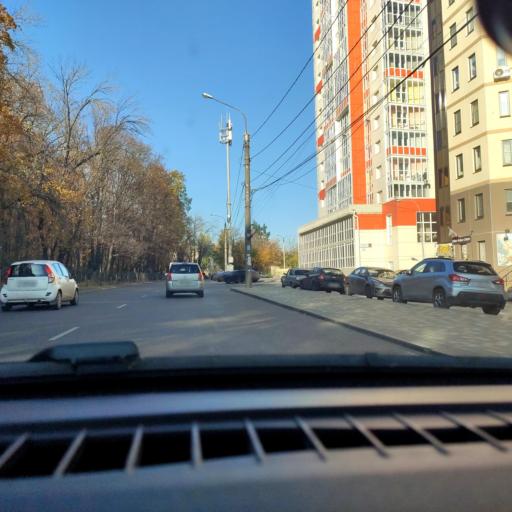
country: RU
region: Voronezj
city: Voronezh
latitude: 51.7089
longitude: 39.2297
